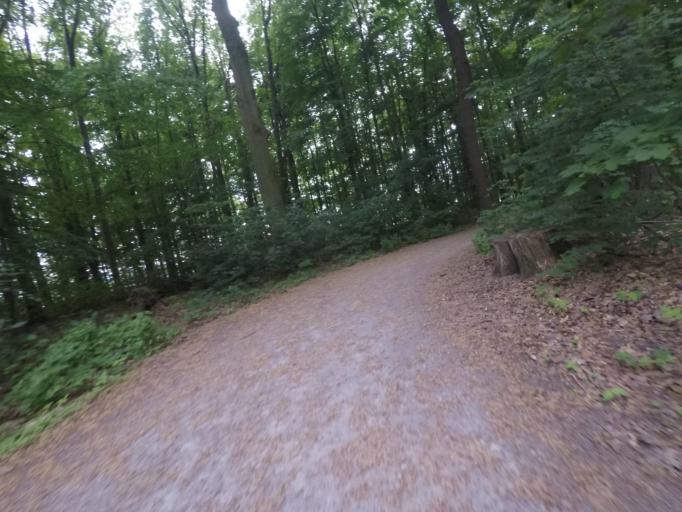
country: DE
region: North Rhine-Westphalia
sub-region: Regierungsbezirk Detmold
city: Bad Salzuflen
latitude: 52.1016
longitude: 8.7231
